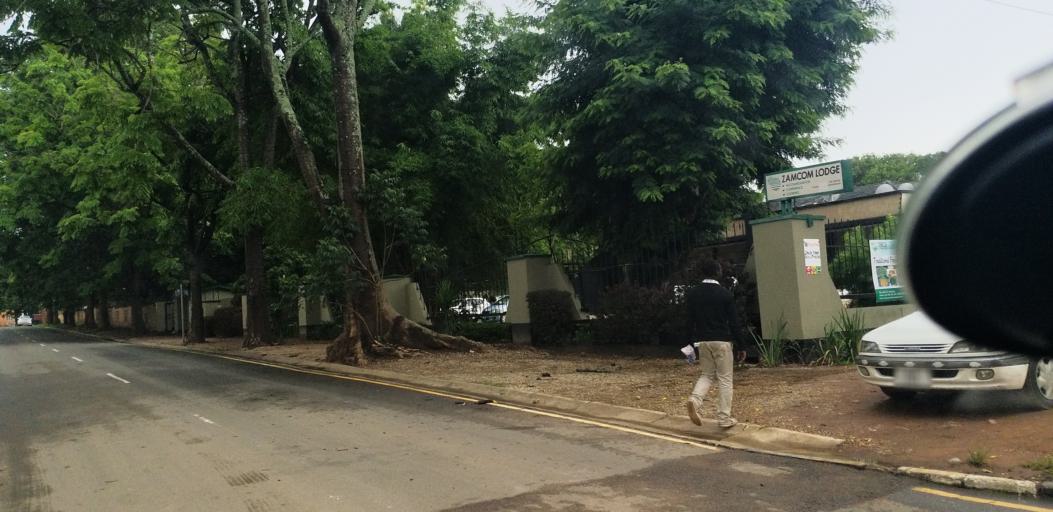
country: ZM
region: Lusaka
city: Lusaka
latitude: -15.4160
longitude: 28.2972
